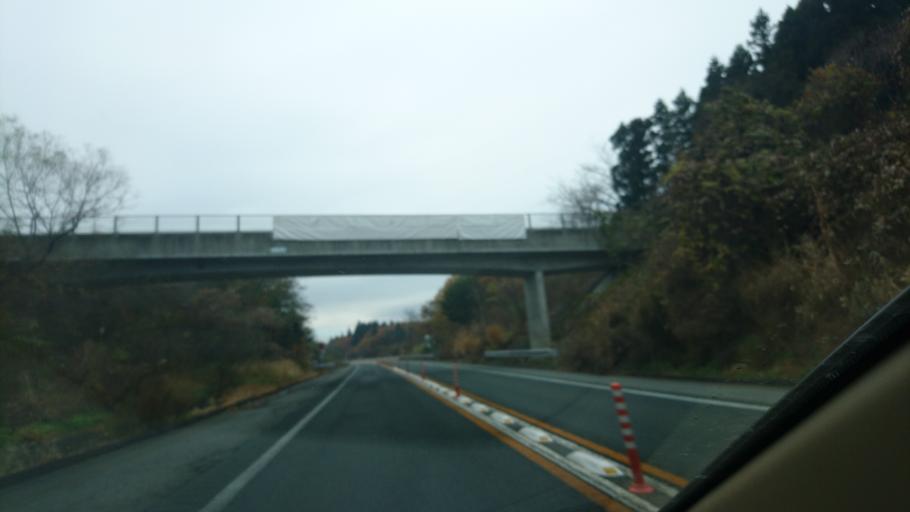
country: JP
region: Iwate
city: Kitakami
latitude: 39.2806
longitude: 141.0133
